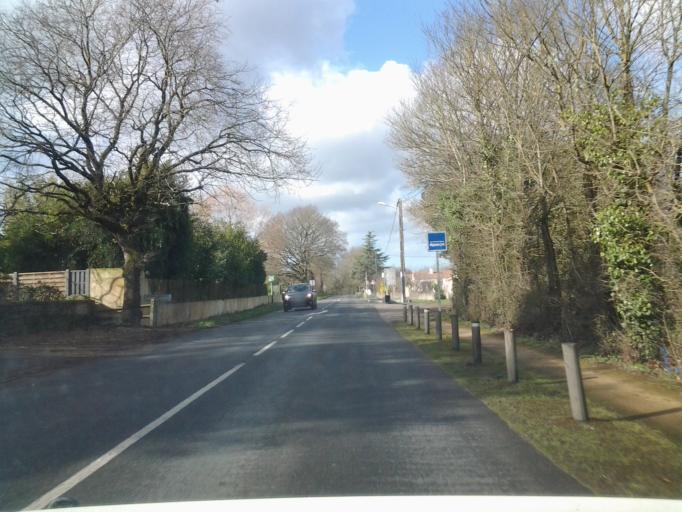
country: FR
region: Pays de la Loire
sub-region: Departement de la Vendee
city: La Roche-sur-Yon
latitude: 46.6405
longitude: -1.4413
